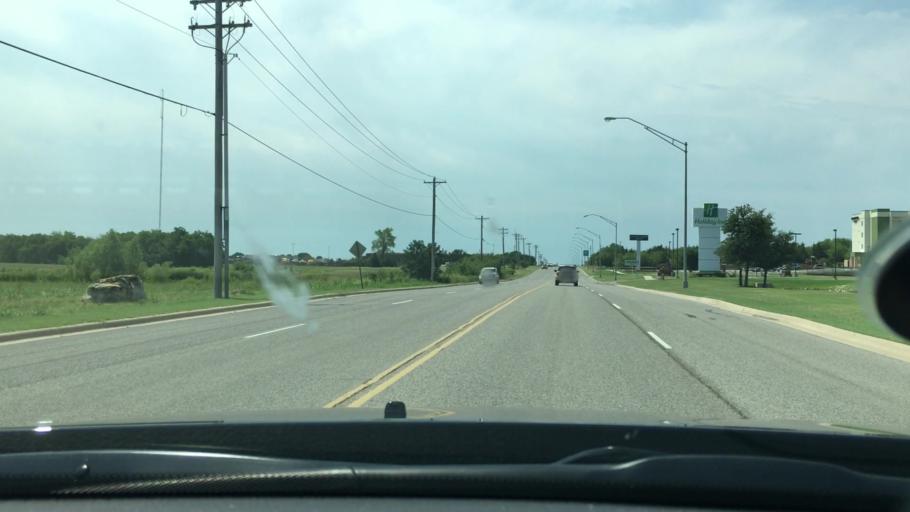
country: US
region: Oklahoma
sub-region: Carter County
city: Ardmore
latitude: 34.1991
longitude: -97.1605
